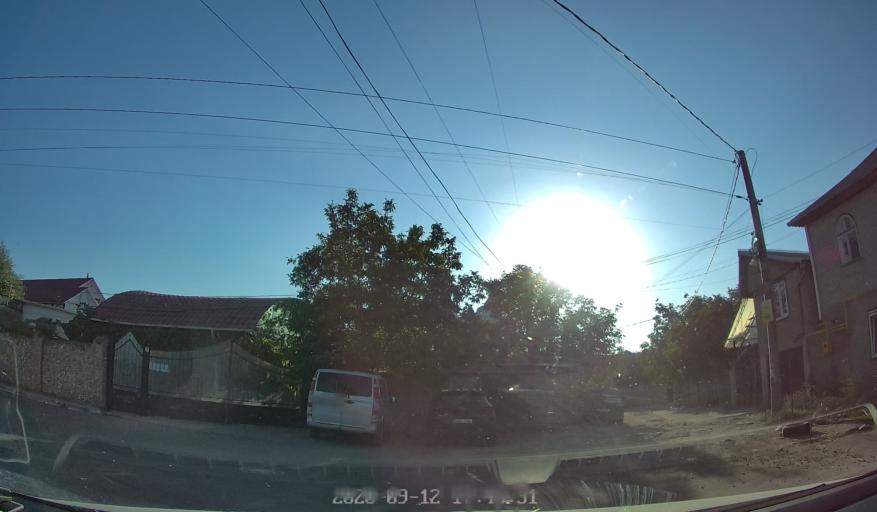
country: MD
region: Chisinau
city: Chisinau
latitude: 47.0165
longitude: 28.8606
